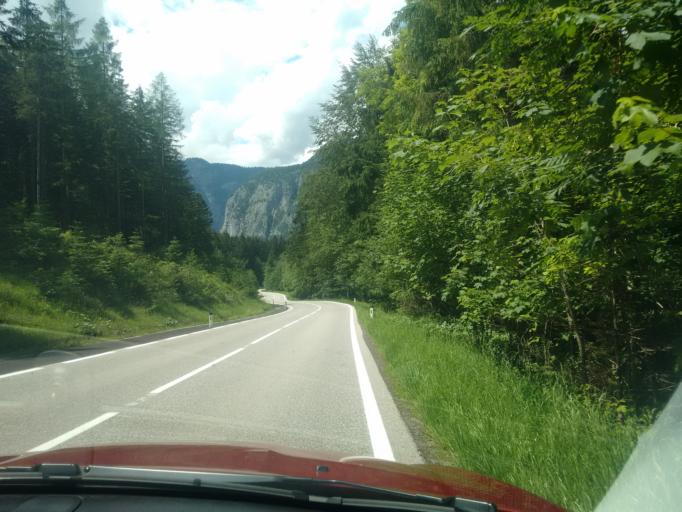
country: AT
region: Styria
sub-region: Politischer Bezirk Liezen
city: Bad Aussee
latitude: 47.5484
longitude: 13.7008
